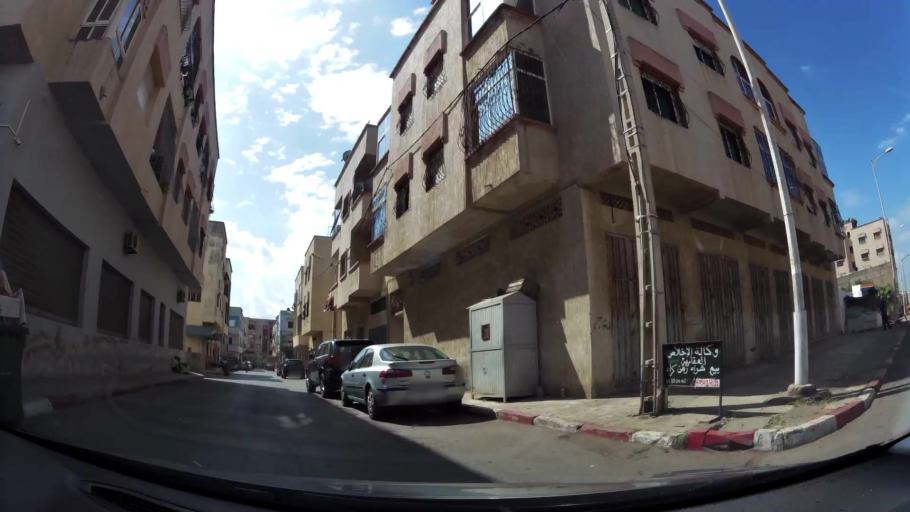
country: MA
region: Rabat-Sale-Zemmour-Zaer
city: Sale
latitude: 34.0626
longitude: -6.8040
